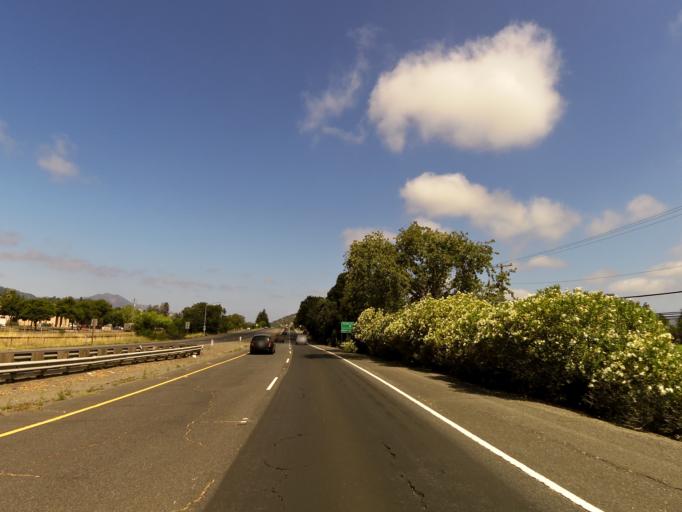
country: US
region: California
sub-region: Napa County
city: Yountville
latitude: 38.3943
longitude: -122.3552
